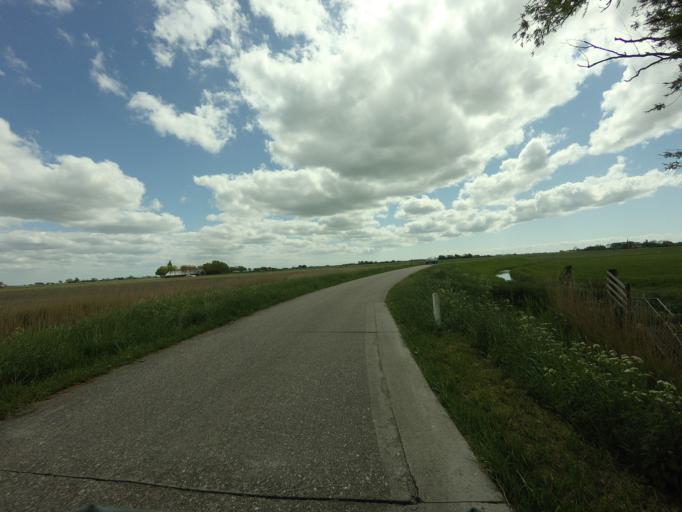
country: NL
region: Friesland
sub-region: Gemeente Littenseradiel
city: Wommels
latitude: 53.1164
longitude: 5.5508
